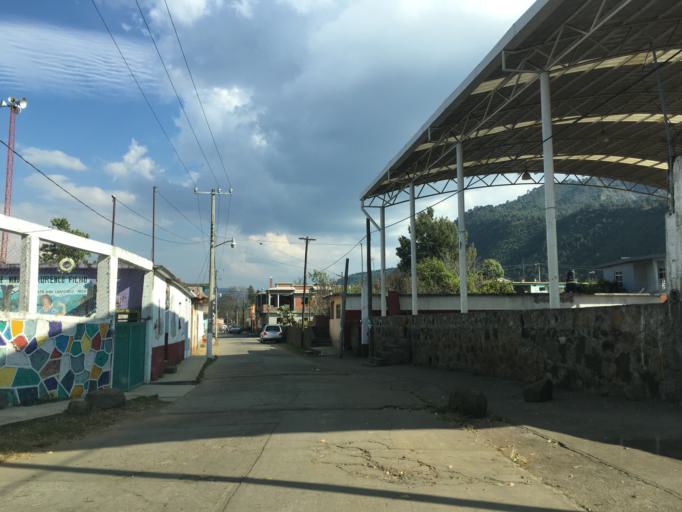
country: MX
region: Michoacan
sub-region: Patzcuaro
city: Santa Ana Chapitiro
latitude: 19.5260
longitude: -101.6532
